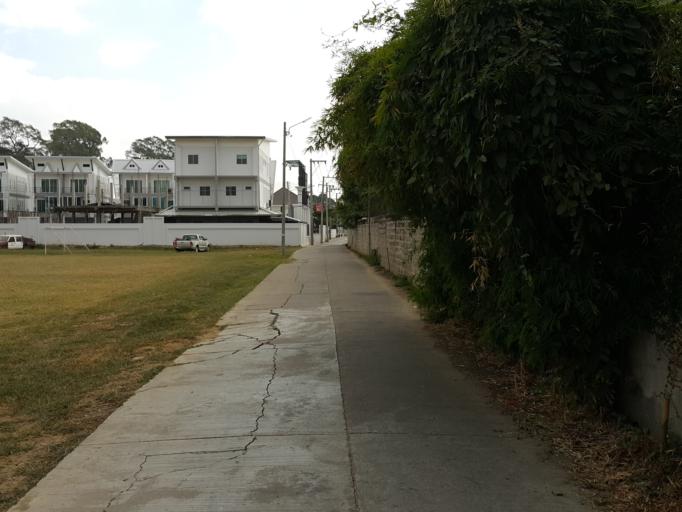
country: TH
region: Chiang Mai
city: Chiang Mai
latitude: 18.7514
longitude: 99.0081
